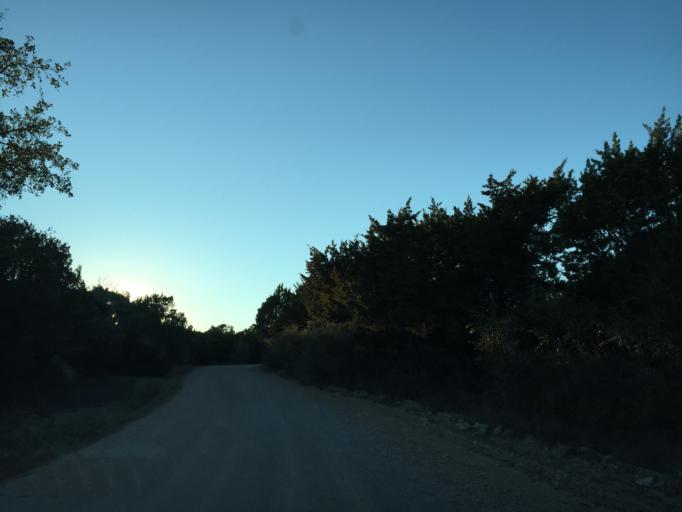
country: US
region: Texas
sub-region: Travis County
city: Lago Vista
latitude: 30.5064
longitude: -97.9822
